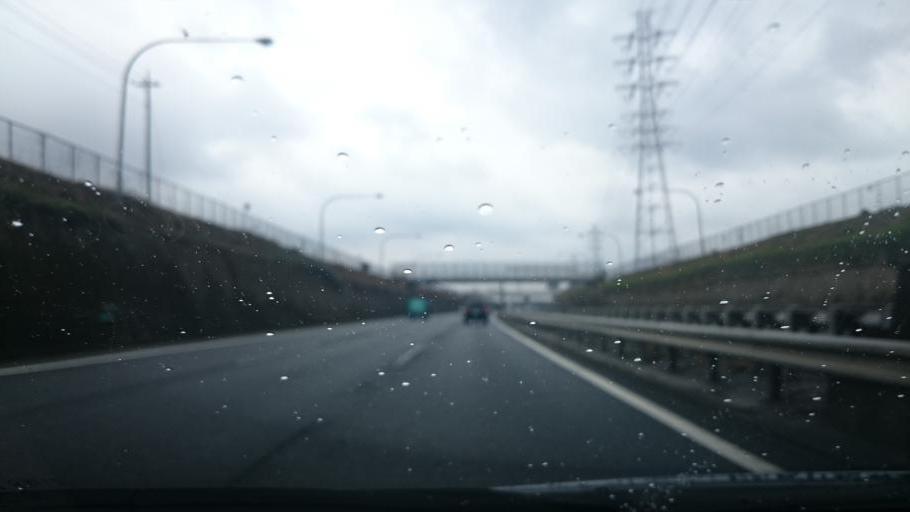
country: JP
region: Saitama
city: Oi
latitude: 35.8299
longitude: 139.5094
